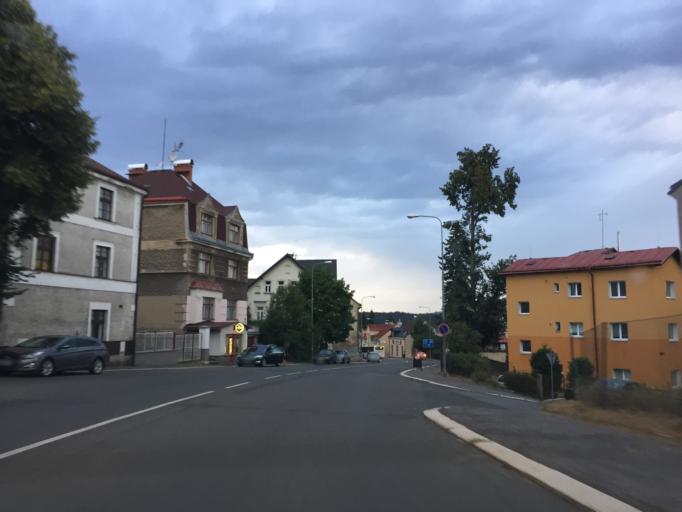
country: CZ
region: Liberecky
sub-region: Okres Jablonec nad Nisou
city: Jablonec nad Nisou
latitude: 50.7161
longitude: 15.1651
